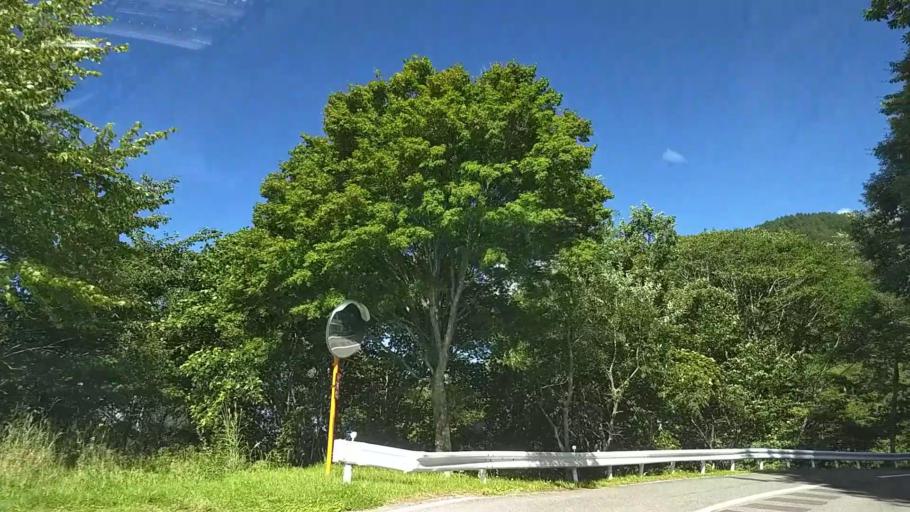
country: JP
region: Nagano
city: Matsumoto
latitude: 36.1965
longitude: 138.1147
